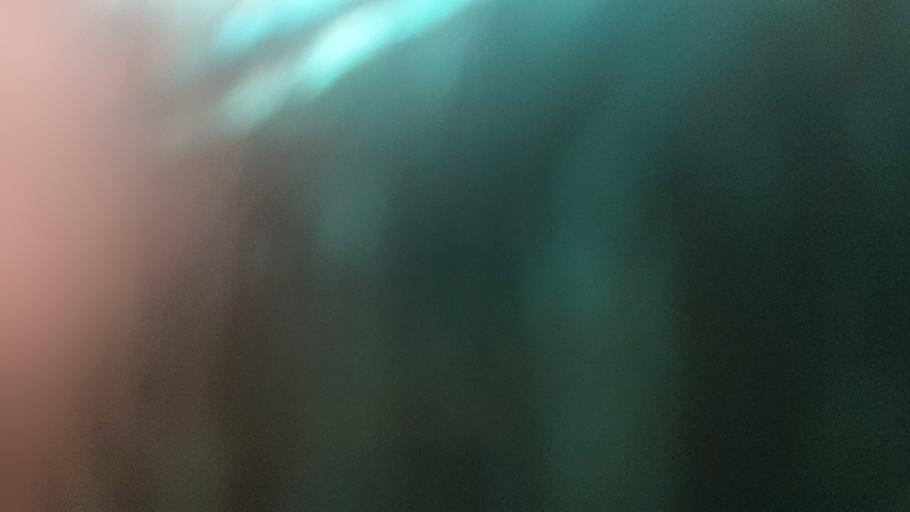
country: TW
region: Taiwan
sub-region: Chiayi
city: Taibao
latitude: 23.7055
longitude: 120.1818
